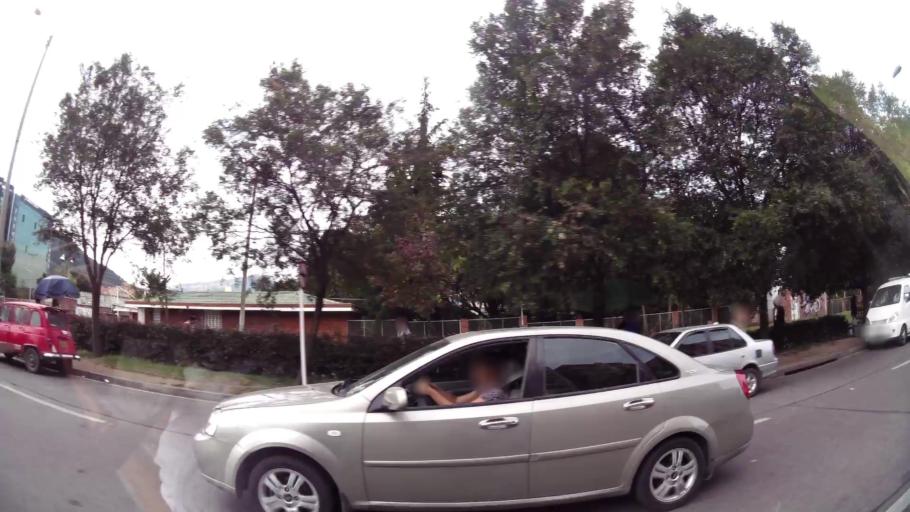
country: CO
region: Bogota D.C.
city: Barrio San Luis
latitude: 4.7122
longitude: -74.0308
